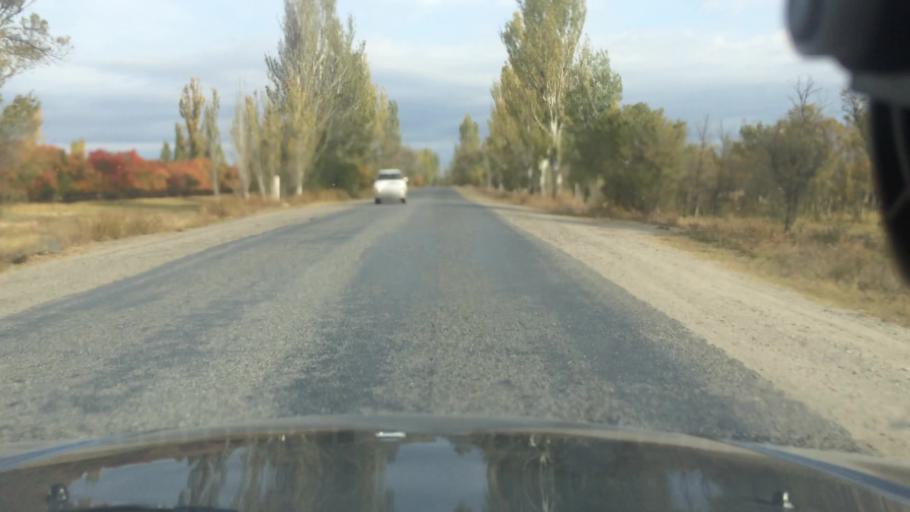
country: KG
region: Ysyk-Koel
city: Karakol
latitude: 42.5692
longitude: 78.3911
